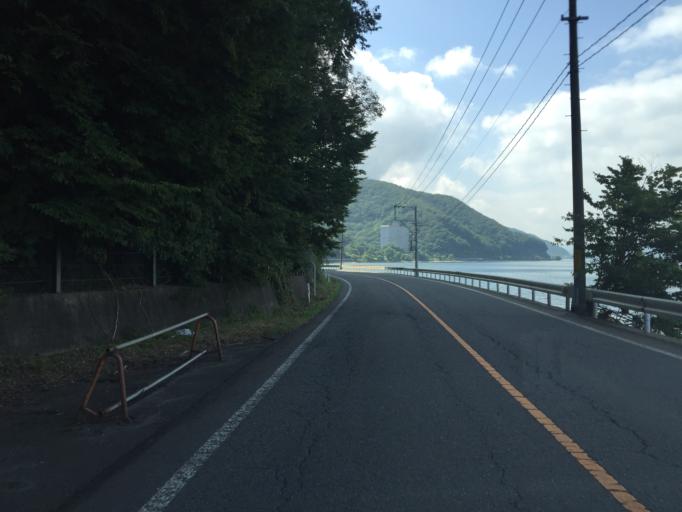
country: JP
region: Fukushima
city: Inawashiro
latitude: 37.4682
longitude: 140.1531
